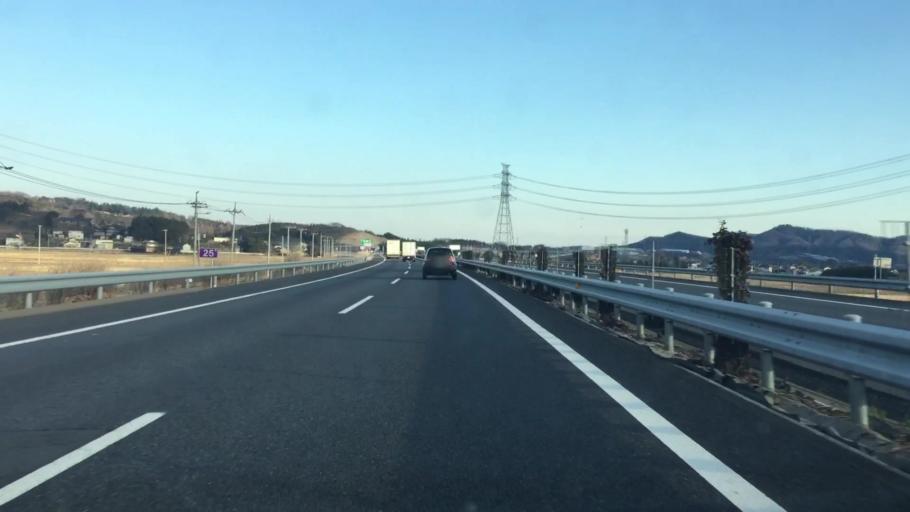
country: JP
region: Gunma
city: Ota
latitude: 36.3439
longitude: 139.3336
